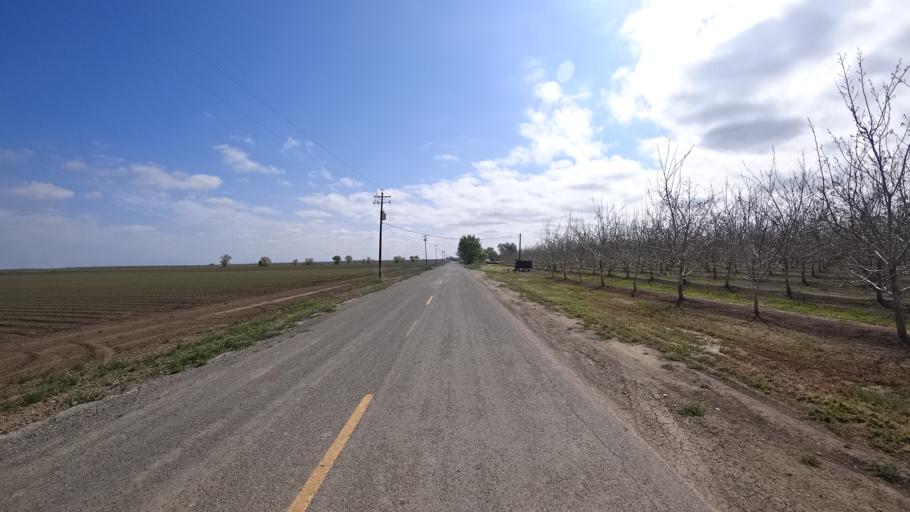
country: US
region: California
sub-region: Colusa County
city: Colusa
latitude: 39.4200
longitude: -121.9565
